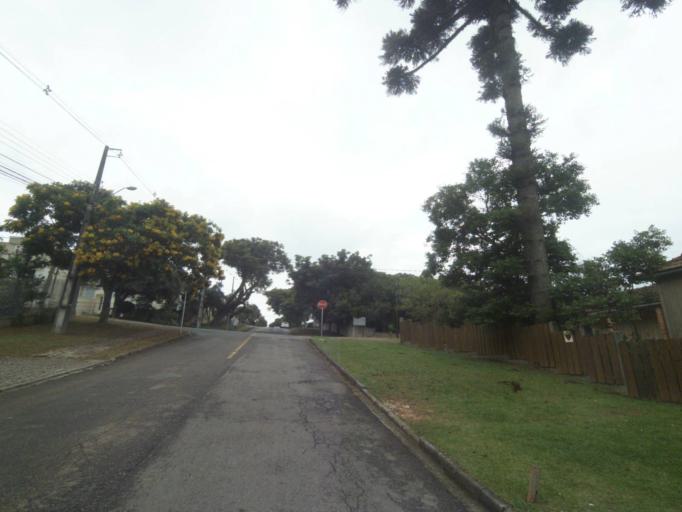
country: BR
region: Parana
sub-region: Curitiba
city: Curitiba
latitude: -25.4124
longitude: -49.2839
